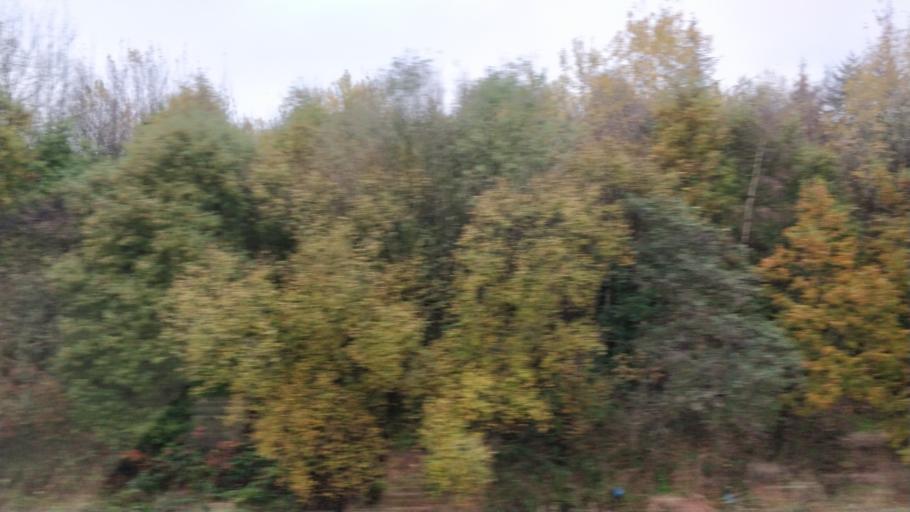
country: GB
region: England
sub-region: Borough of Wigan
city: Shevington
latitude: 53.5548
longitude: -2.6635
